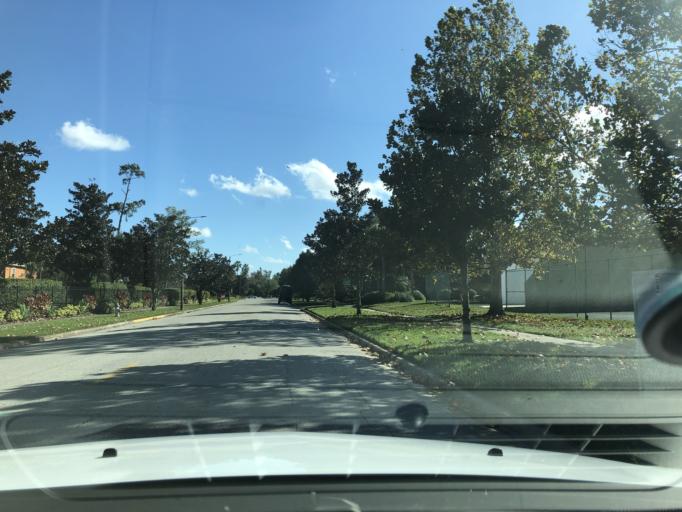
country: US
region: Florida
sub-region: Orange County
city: Oak Ridge
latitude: 28.4980
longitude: -81.4500
